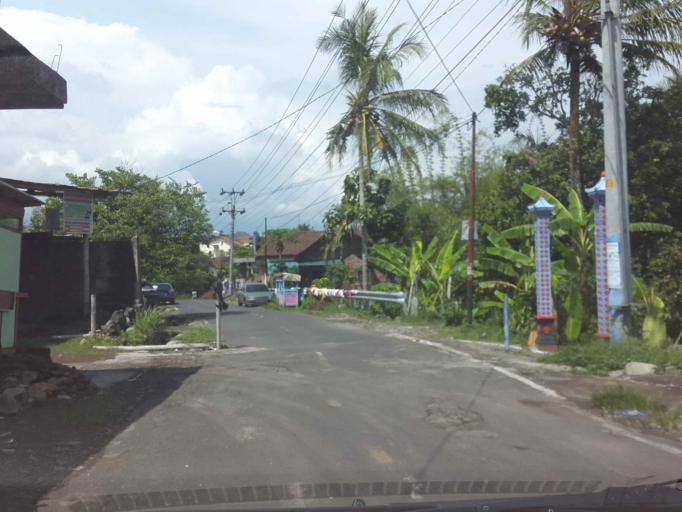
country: ID
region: Central Java
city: Salatiga
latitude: -7.3215
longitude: 110.5098
